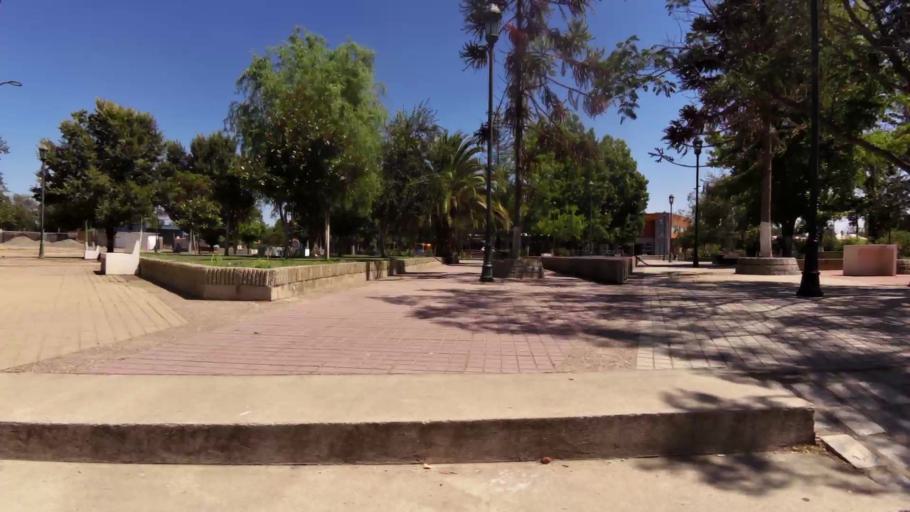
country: CL
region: Maule
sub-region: Provincia de Talca
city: Talca
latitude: -35.3050
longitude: -71.5153
